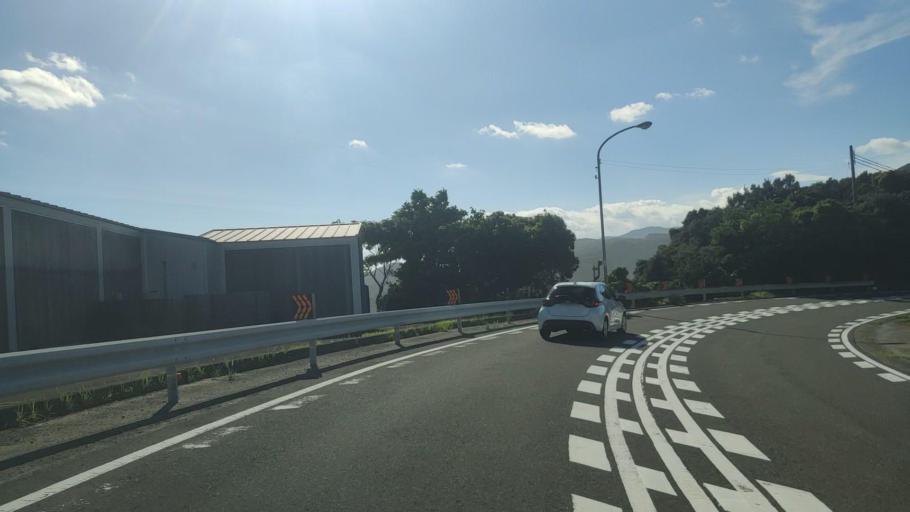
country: JP
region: Wakayama
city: Tanabe
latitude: 33.5060
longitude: 135.6368
